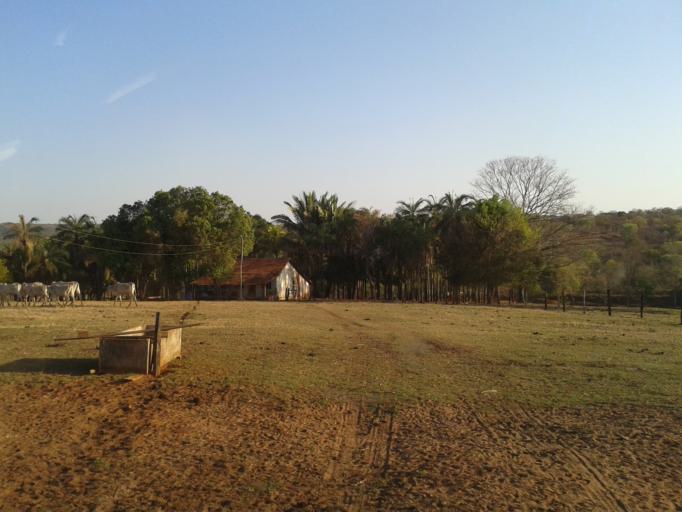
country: BR
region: Minas Gerais
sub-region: Campina Verde
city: Campina Verde
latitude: -19.2665
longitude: -49.6057
